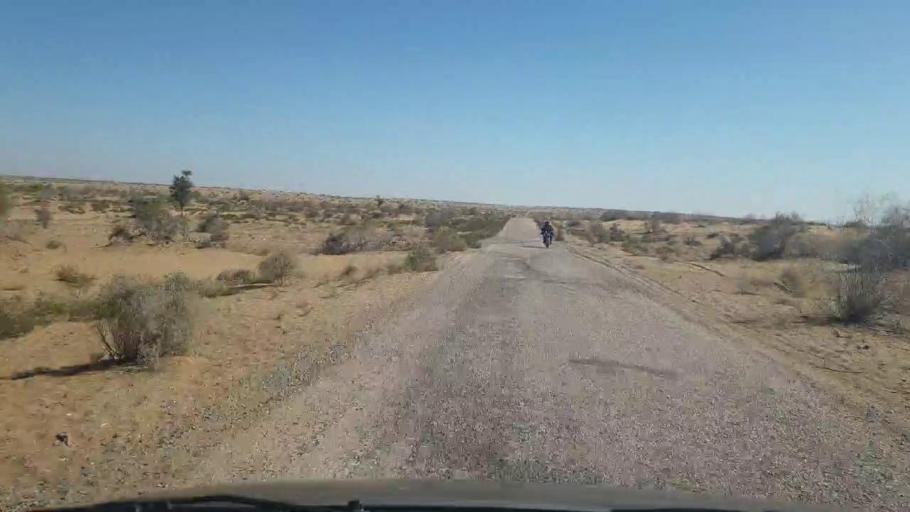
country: PK
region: Sindh
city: Bozdar
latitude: 27.0131
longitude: 68.7895
